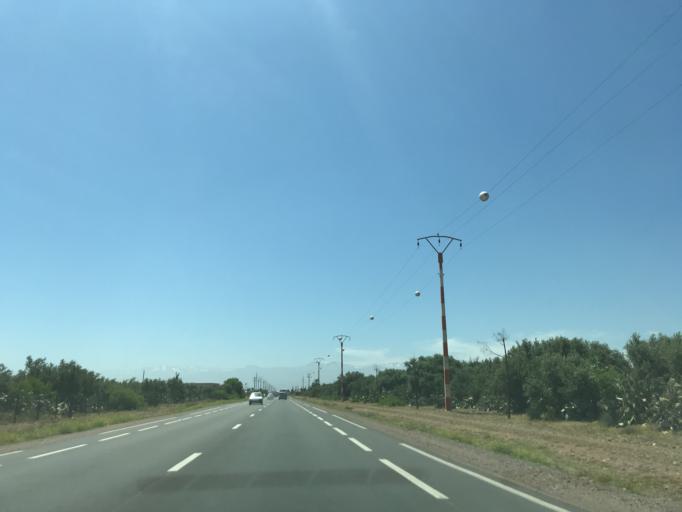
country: MA
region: Marrakech-Tensift-Al Haouz
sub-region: Marrakech
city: Marrakesh
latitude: 31.5394
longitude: -7.9997
